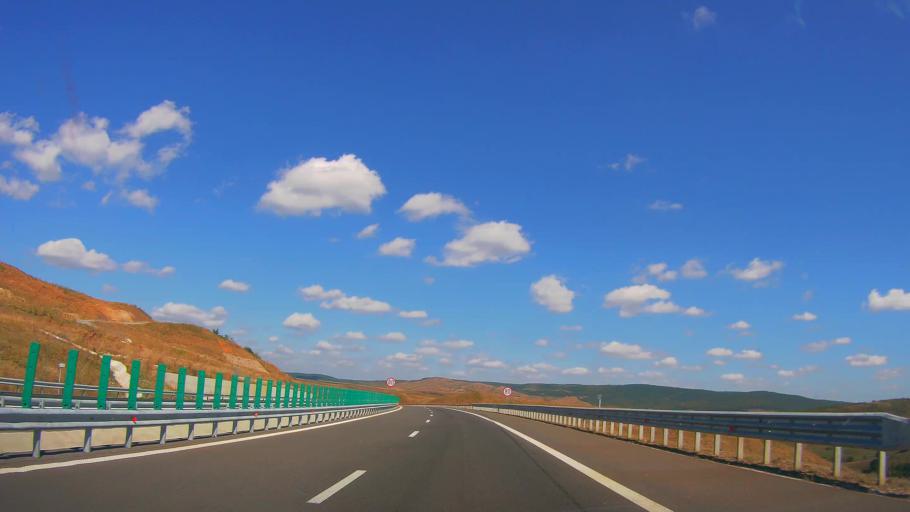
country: RO
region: Cluj
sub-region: Comuna Baciu
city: Mera
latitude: 46.7975
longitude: 23.4254
